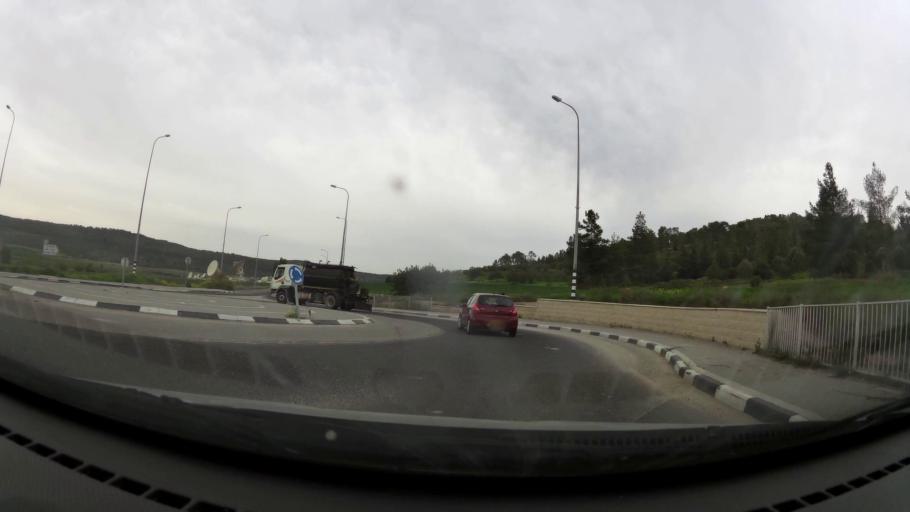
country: IL
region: Jerusalem
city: Bet Shemesh
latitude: 31.6828
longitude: 35.0021
